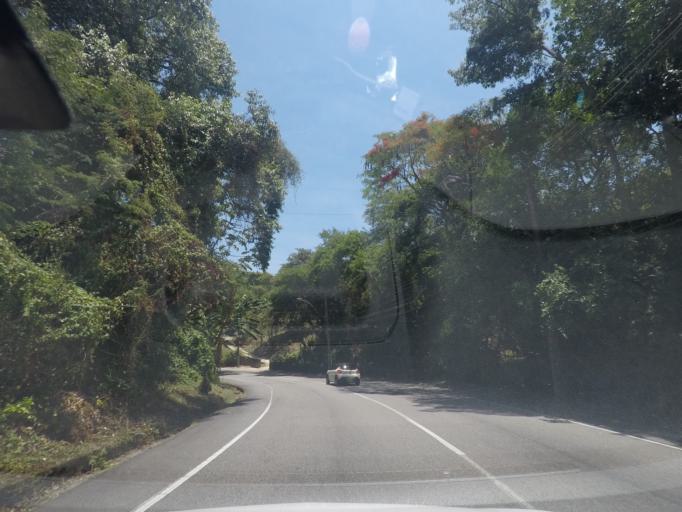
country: BR
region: Rio de Janeiro
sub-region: Niteroi
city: Niteroi
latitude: -22.9228
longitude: -43.0667
